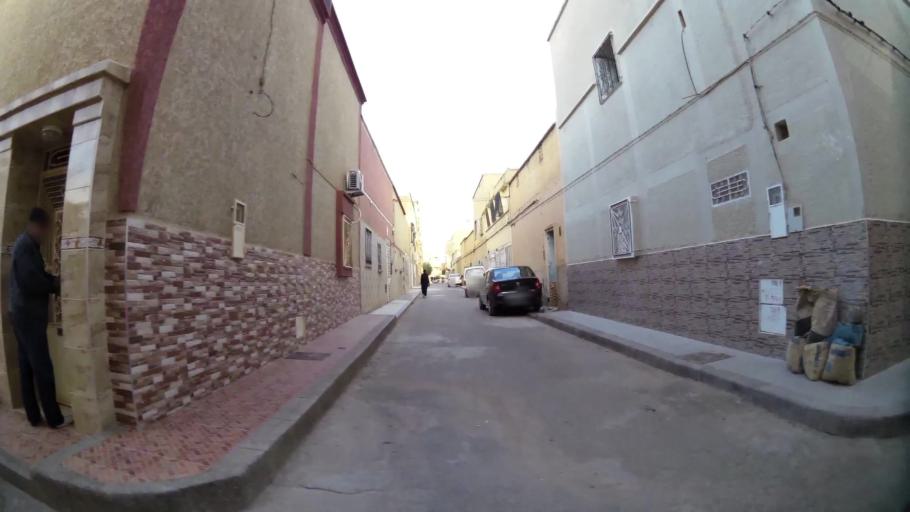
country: MA
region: Oriental
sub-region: Oujda-Angad
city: Oujda
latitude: 34.6782
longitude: -1.8832
